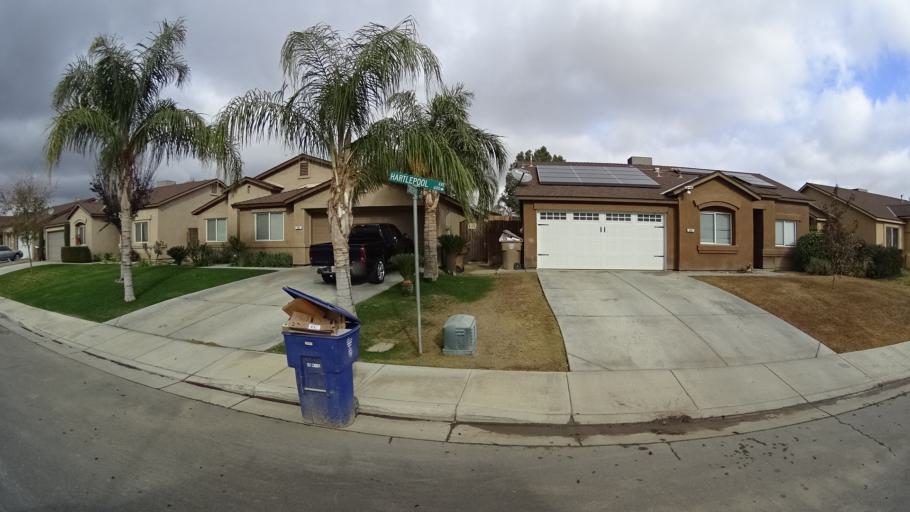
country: US
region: California
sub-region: Kern County
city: Greenfield
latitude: 35.2945
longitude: -118.9978
